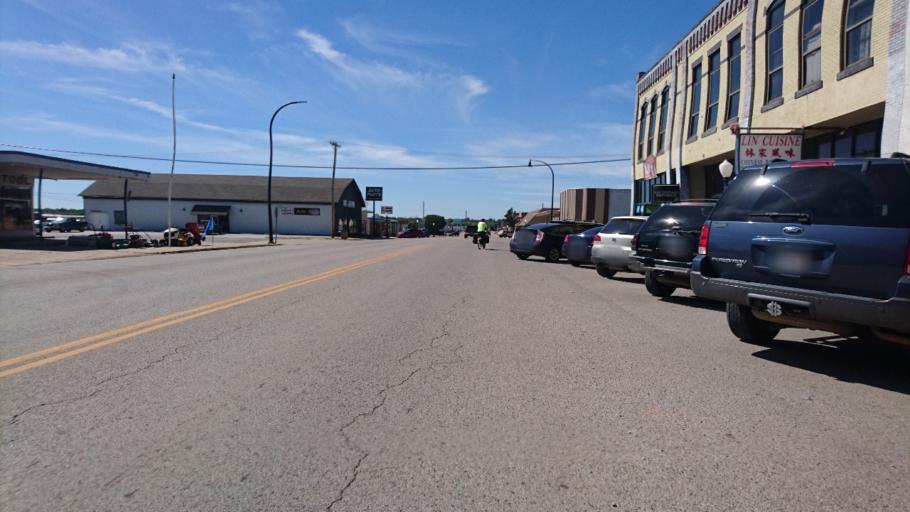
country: US
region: Oklahoma
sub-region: Lincoln County
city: Stroud
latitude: 35.7491
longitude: -96.6584
